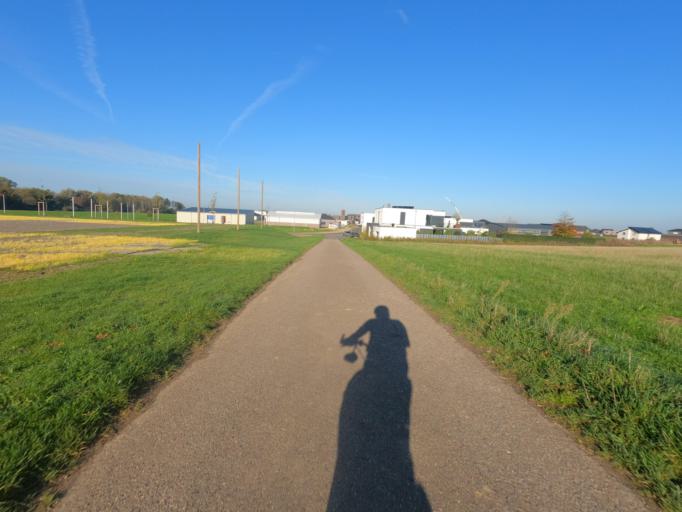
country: DE
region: North Rhine-Westphalia
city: Erkelenz
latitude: 51.0944
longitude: 6.3398
